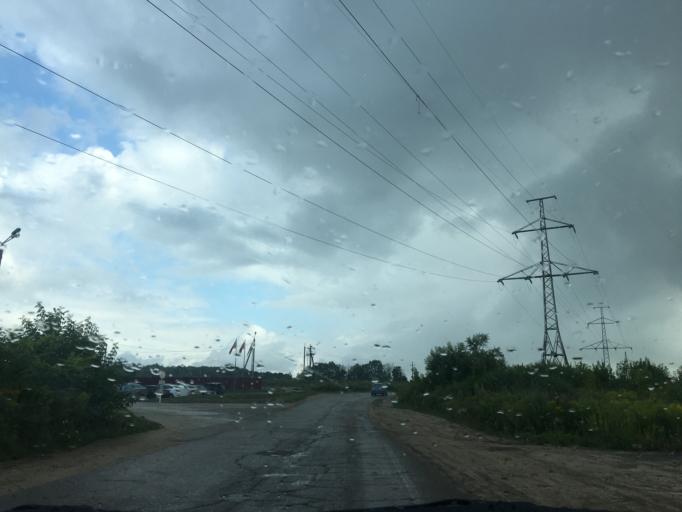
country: RU
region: Tula
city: Mendeleyevskiy
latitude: 54.1234
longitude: 37.6022
